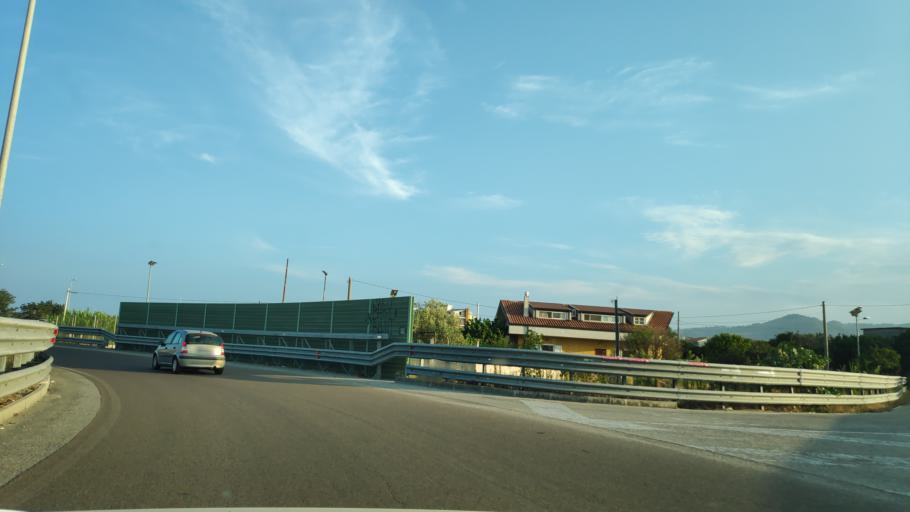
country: IT
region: Calabria
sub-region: Provincia di Catanzaro
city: Marina di Davoli
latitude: 38.6721
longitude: 16.5468
